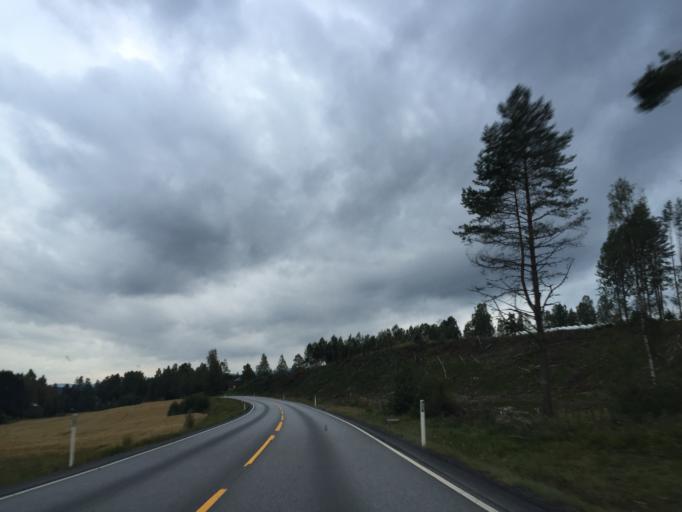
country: NO
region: Hedmark
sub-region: Nord-Odal
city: Sand
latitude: 60.4462
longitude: 11.4971
